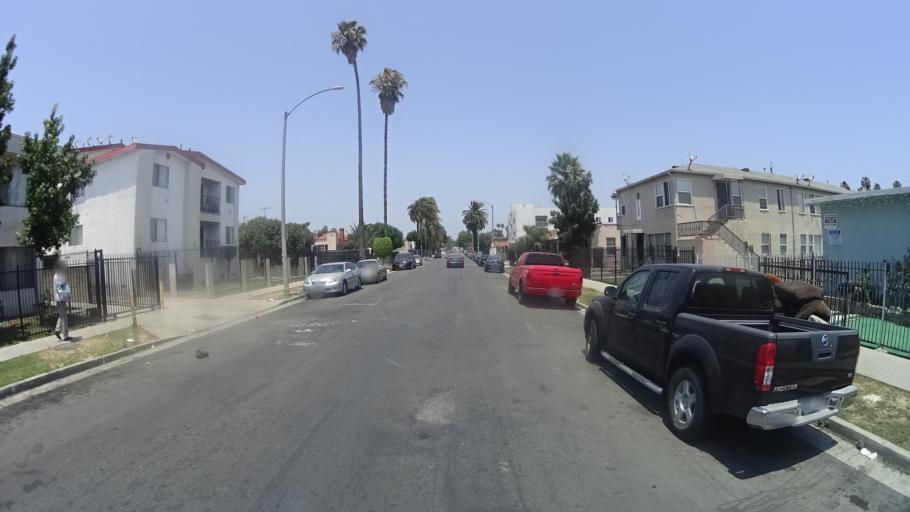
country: US
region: California
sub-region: Los Angeles County
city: View Park-Windsor Hills
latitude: 33.9810
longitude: -118.3338
